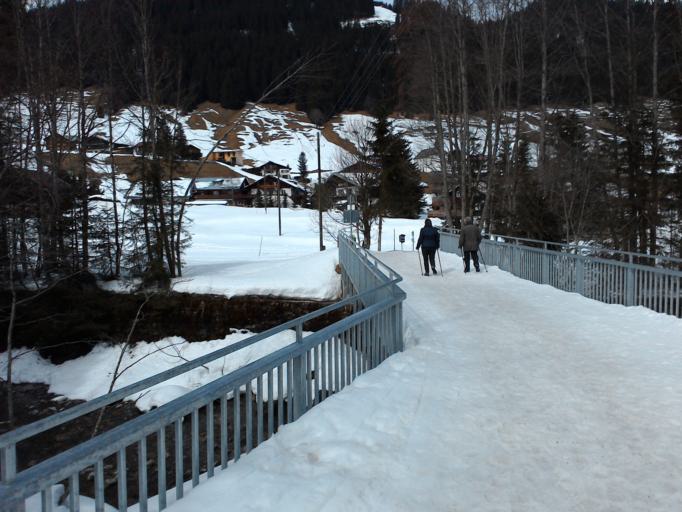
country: AT
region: Vorarlberg
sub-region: Politischer Bezirk Bregenz
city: Mittelberg
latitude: 47.3087
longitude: 10.1212
